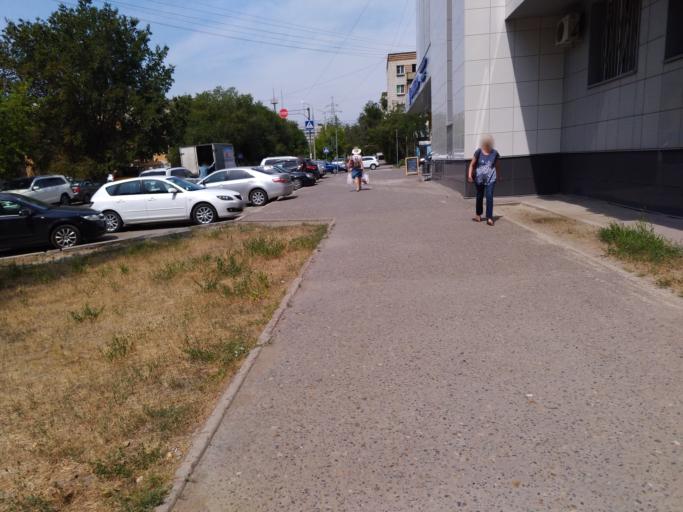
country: RU
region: Volgograd
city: Volgograd
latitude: 48.6982
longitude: 44.4937
